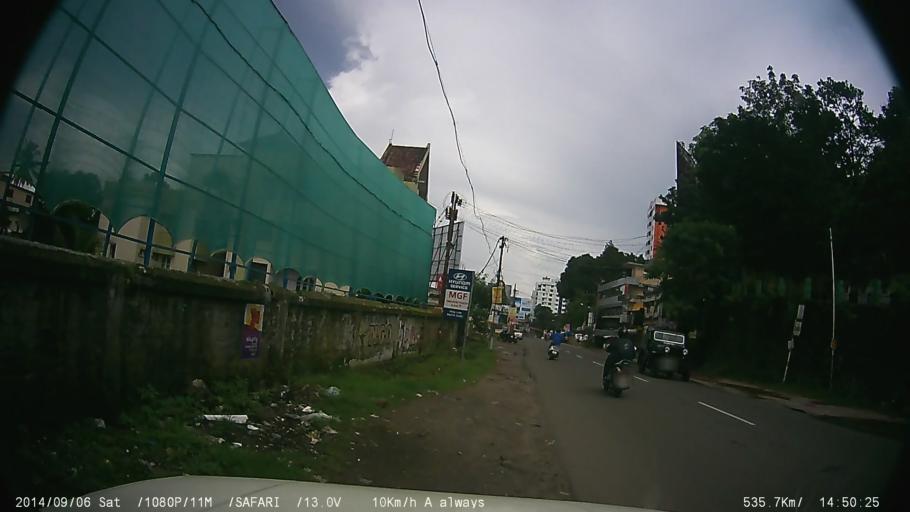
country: IN
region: Kerala
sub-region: Kottayam
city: Kottayam
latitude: 9.5875
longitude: 76.5447
